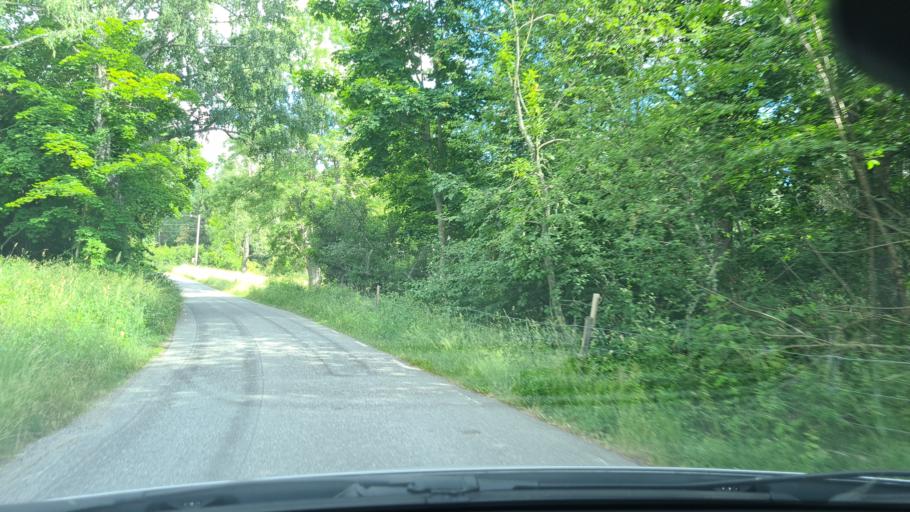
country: SE
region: Stockholm
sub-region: Vaxholms Kommun
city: Vaxholm
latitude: 59.4140
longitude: 18.4374
